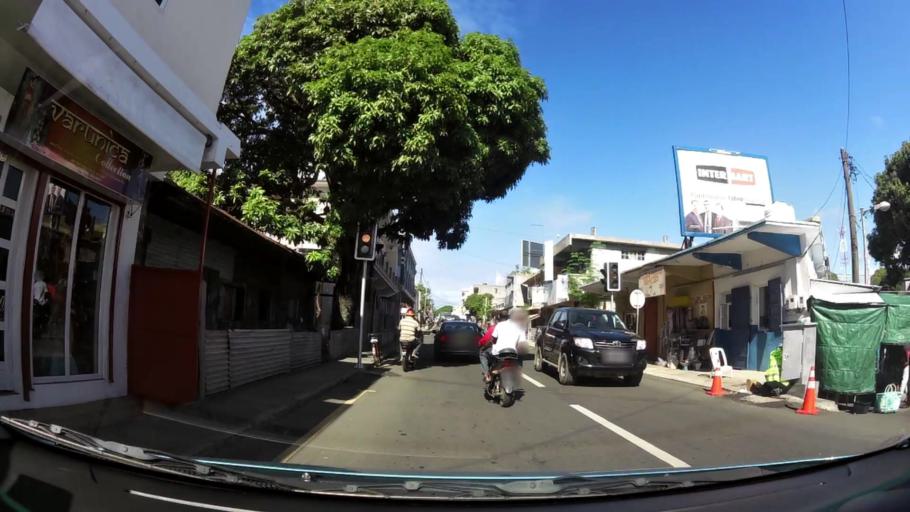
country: MU
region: Grand Port
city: Mahebourg
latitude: -20.4105
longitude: 57.7063
